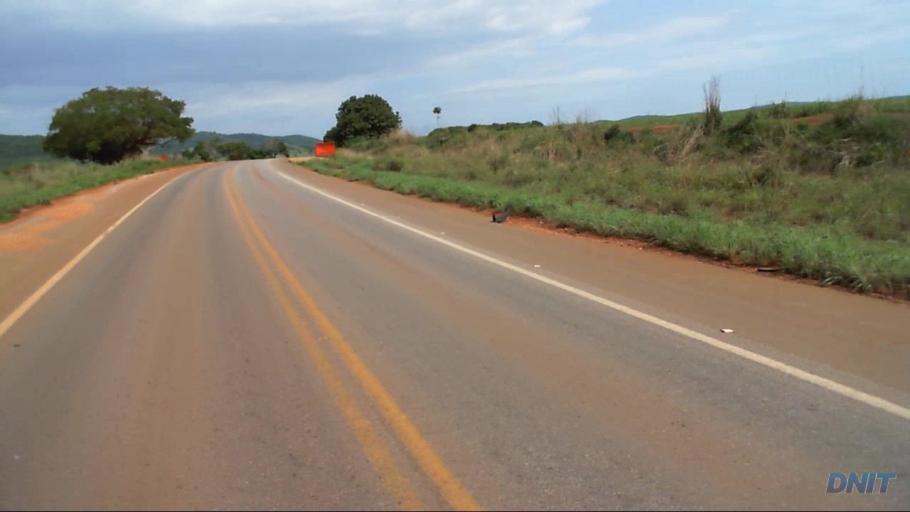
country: BR
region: Goias
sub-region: Barro Alto
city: Barro Alto
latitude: -15.0503
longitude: -48.8861
